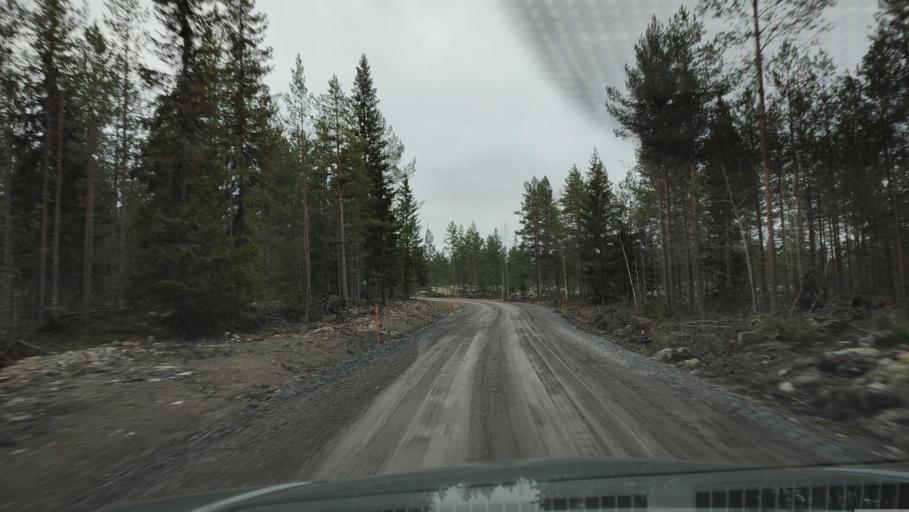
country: FI
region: Southern Ostrobothnia
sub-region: Suupohja
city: Karijoki
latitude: 62.2018
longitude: 21.5879
